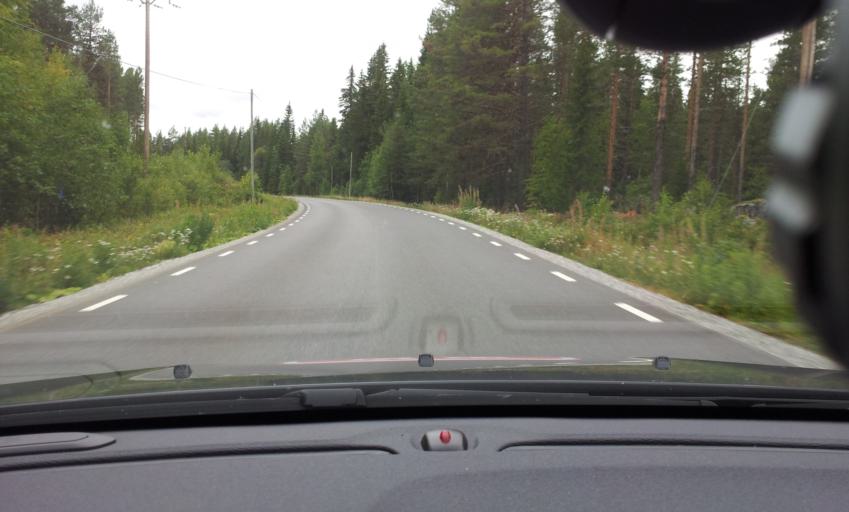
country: SE
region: Jaemtland
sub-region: Braecke Kommun
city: Braecke
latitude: 63.0682
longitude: 15.3504
